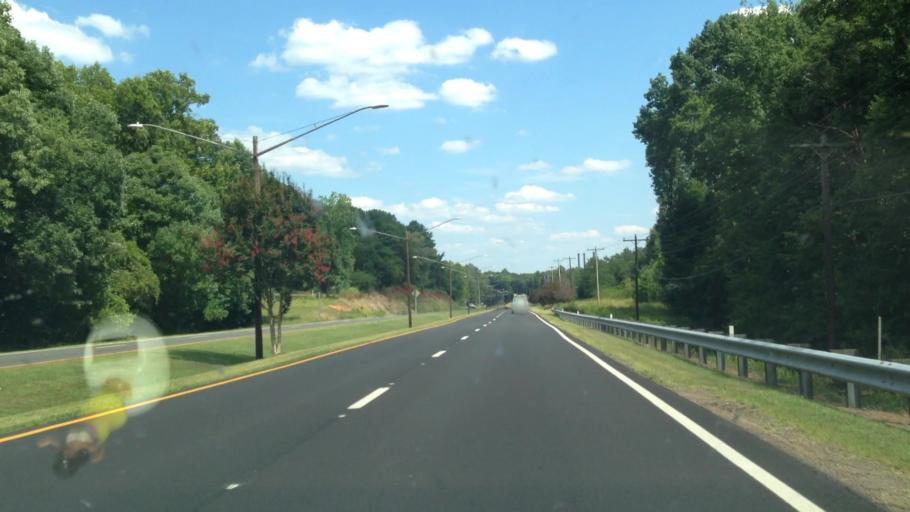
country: US
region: Virginia
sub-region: City of Danville
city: Danville
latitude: 36.5850
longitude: -79.4471
